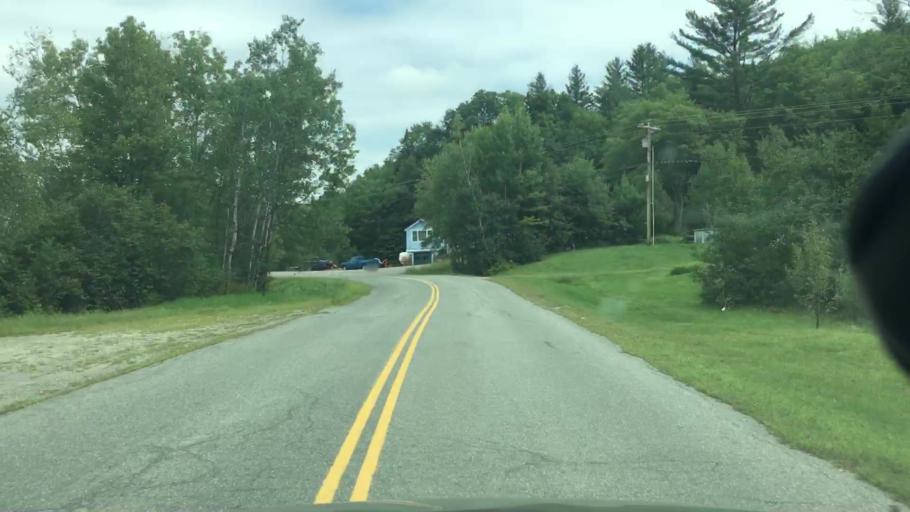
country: US
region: Massachusetts
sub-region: Franklin County
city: Colrain
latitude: 42.7834
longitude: -72.7683
